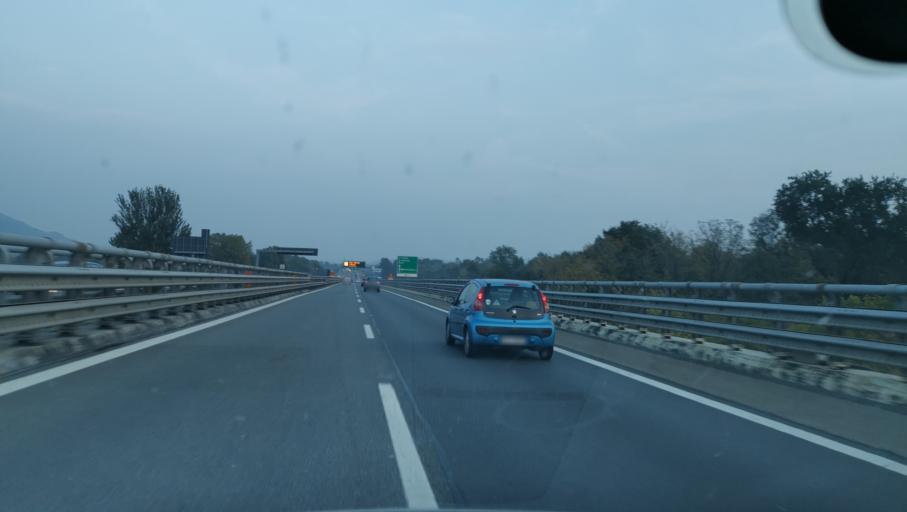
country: IT
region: Piedmont
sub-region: Provincia di Torino
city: Drubiaglio-Grangia
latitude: 45.0929
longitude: 7.4052
